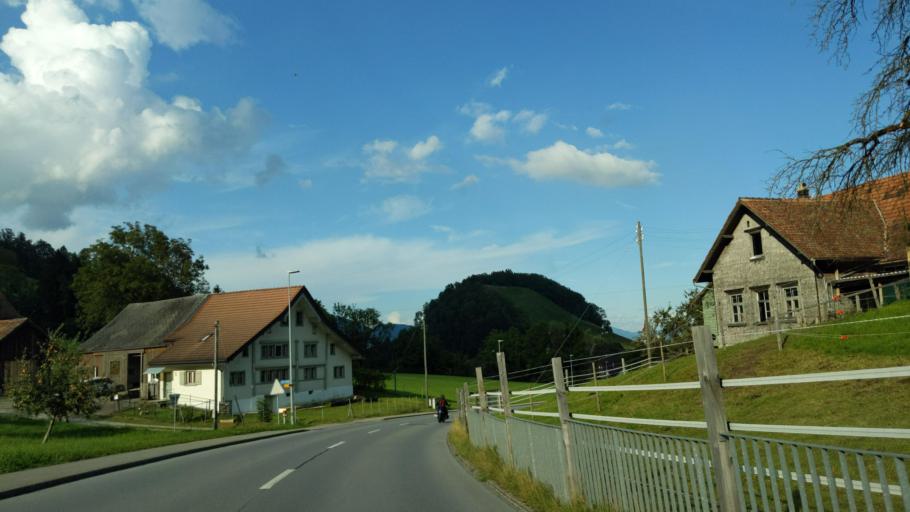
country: CH
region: Saint Gallen
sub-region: Wahlkreis Rheintal
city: Eichberg
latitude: 47.3435
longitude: 9.5198
